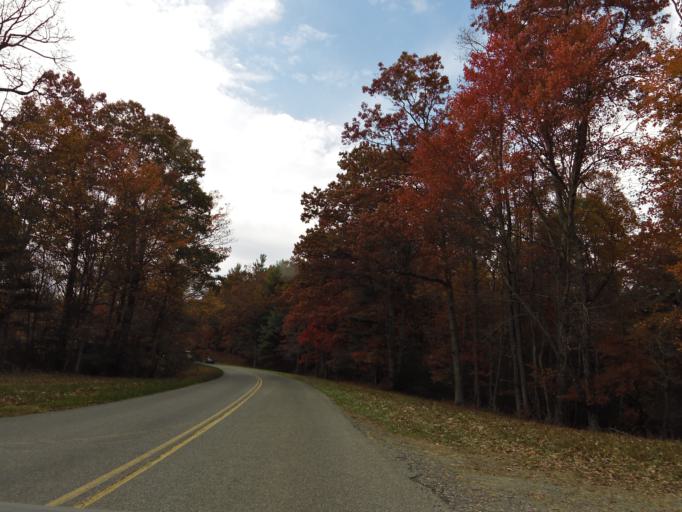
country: US
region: Virginia
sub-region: City of Galax
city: Galax
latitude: 36.5710
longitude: -80.8658
